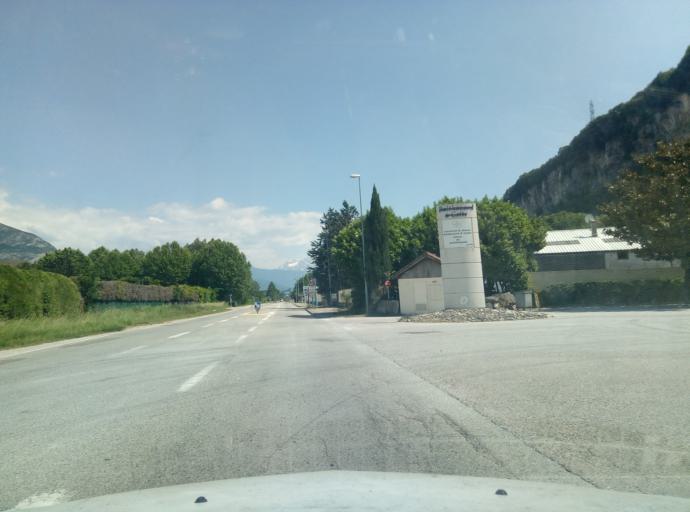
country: FR
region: Rhone-Alpes
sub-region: Departement de l'Isere
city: Fontanil-Cornillon
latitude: 45.2302
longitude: 5.6481
